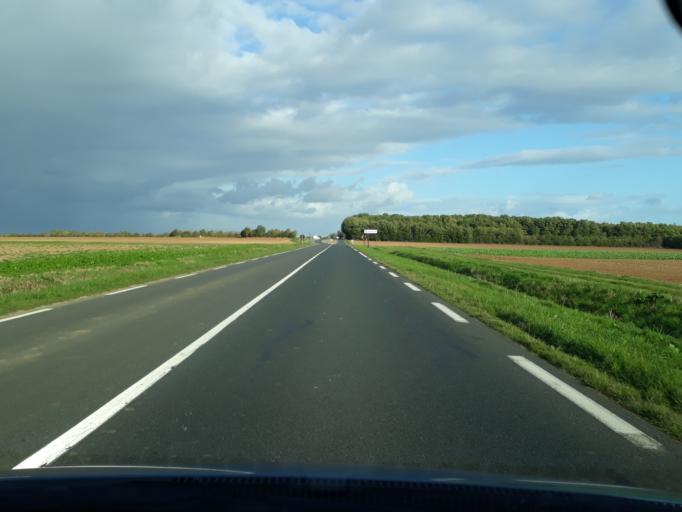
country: FR
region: Ile-de-France
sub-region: Departement de Seine-et-Marne
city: La Chapelle-la-Reine
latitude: 48.3066
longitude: 2.5193
